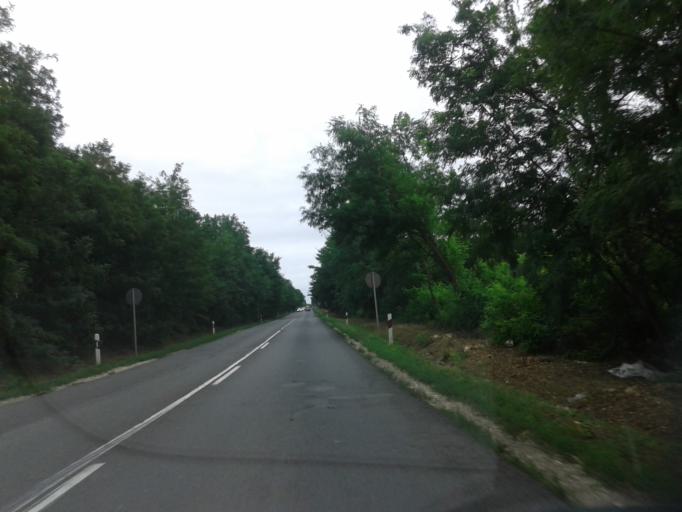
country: HU
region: Pest
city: Kiskunlachaza
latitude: 47.2394
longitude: 19.0206
